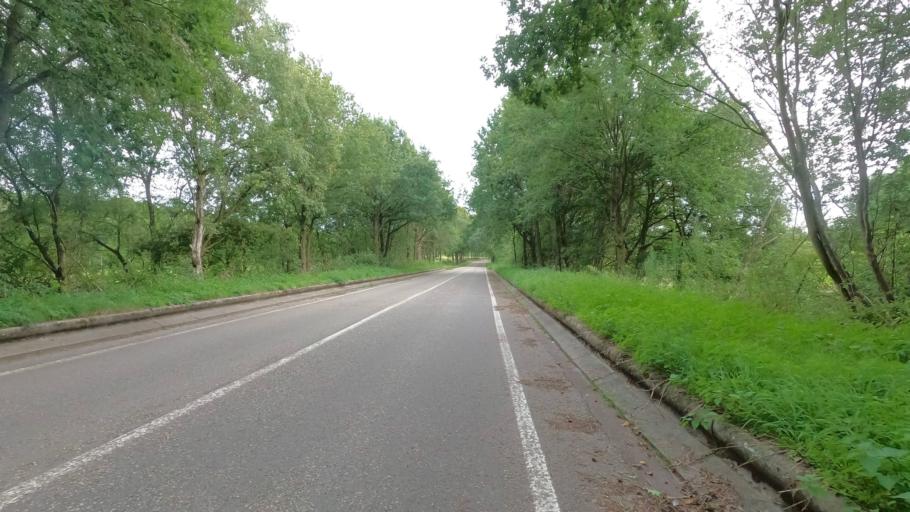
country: BE
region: Flanders
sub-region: Provincie Antwerpen
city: Lille
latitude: 51.2497
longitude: 4.7930
